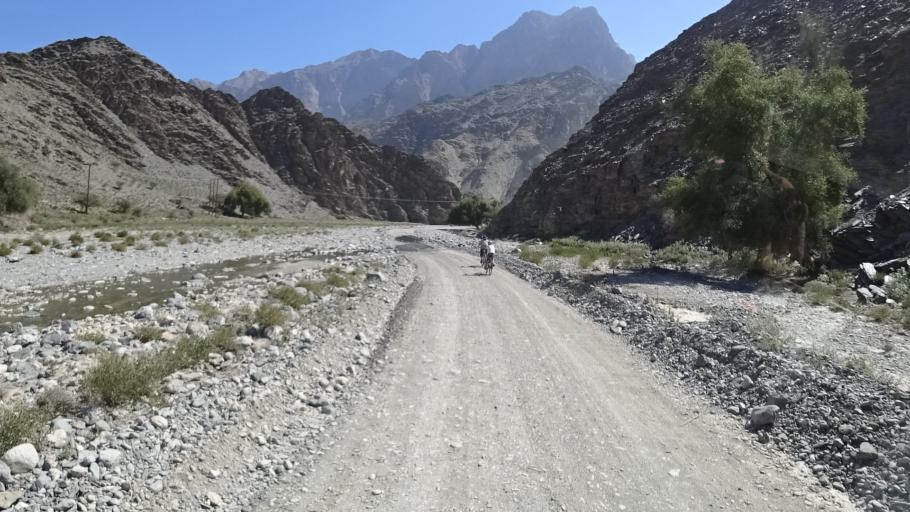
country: OM
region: Al Batinah
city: Bayt al `Awabi
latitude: 23.2595
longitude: 57.4374
